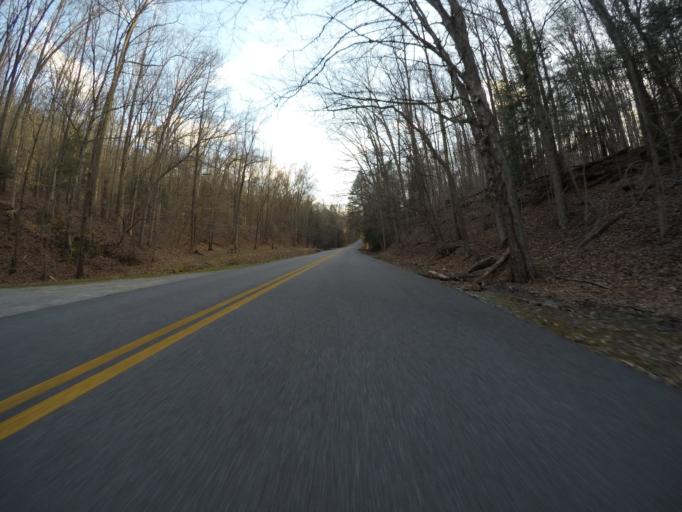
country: US
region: West Virginia
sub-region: Kanawha County
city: Charleston
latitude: 38.3806
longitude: -81.5817
